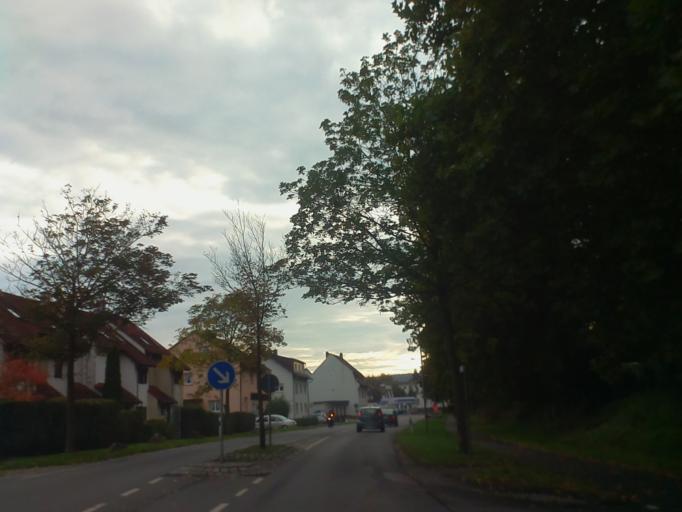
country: DE
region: Hesse
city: Hochst im Odenwald
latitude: 49.8044
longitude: 8.9997
